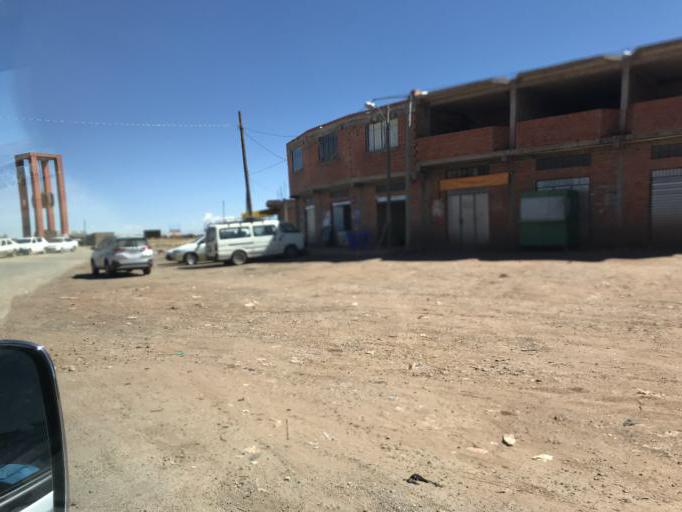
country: BO
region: La Paz
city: Tiahuanaco
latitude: -16.5712
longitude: -68.6733
